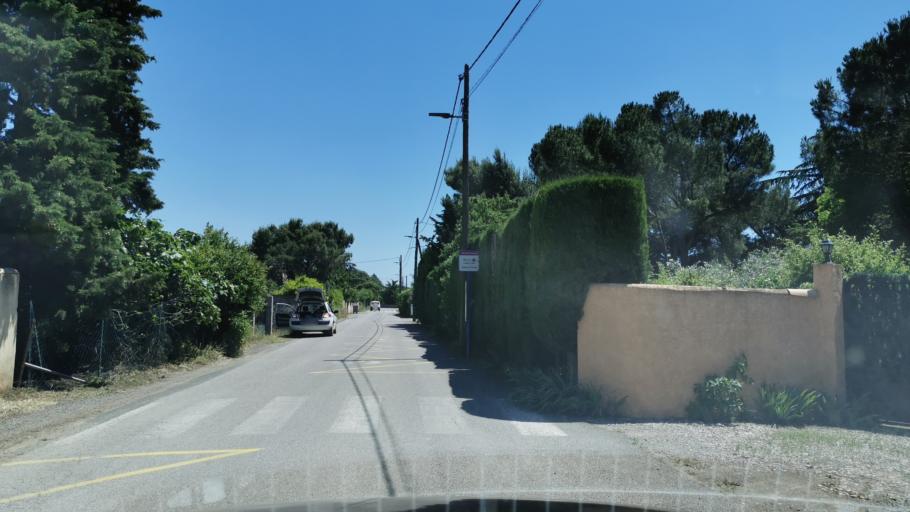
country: FR
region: Languedoc-Roussillon
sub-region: Departement de l'Aude
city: Ouveillan
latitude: 43.2603
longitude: 3.0100
